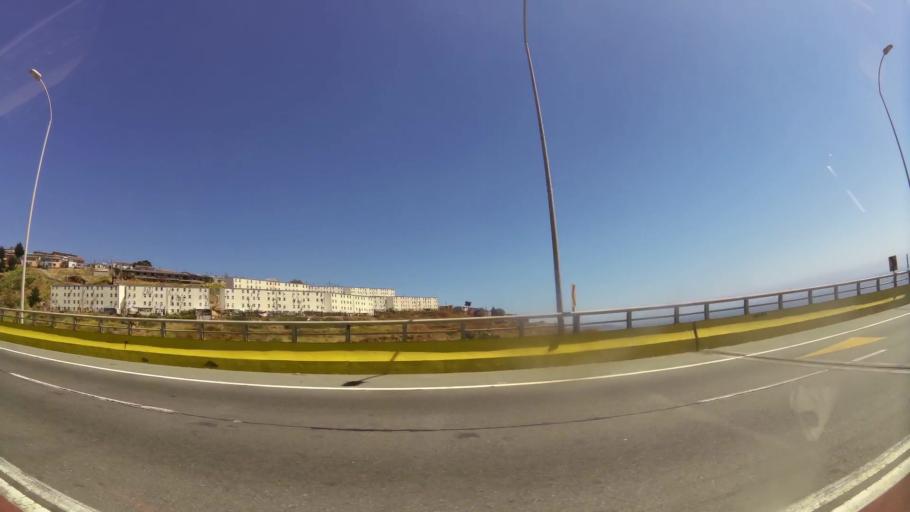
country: CL
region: Valparaiso
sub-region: Provincia de Valparaiso
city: Valparaiso
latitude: -33.0373
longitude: -71.6550
